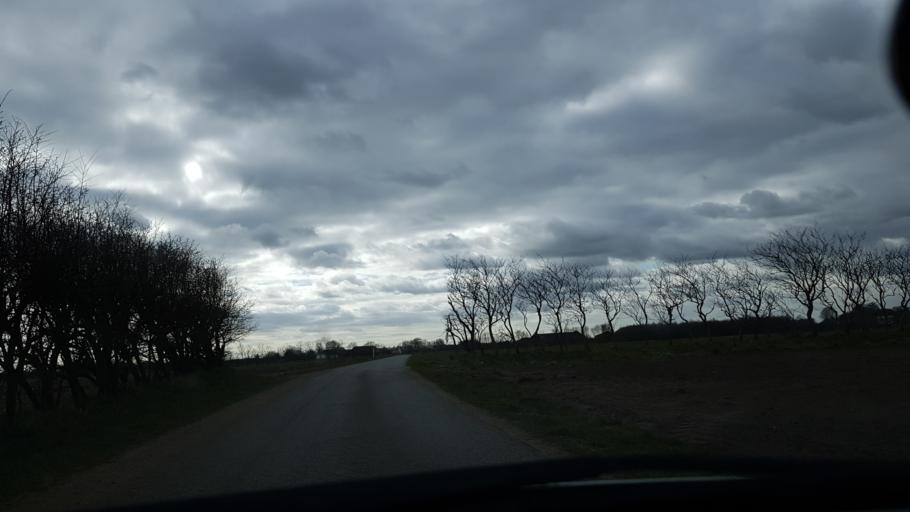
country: DK
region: South Denmark
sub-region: Vejen Kommune
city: Holsted
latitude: 55.4051
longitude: 8.8933
